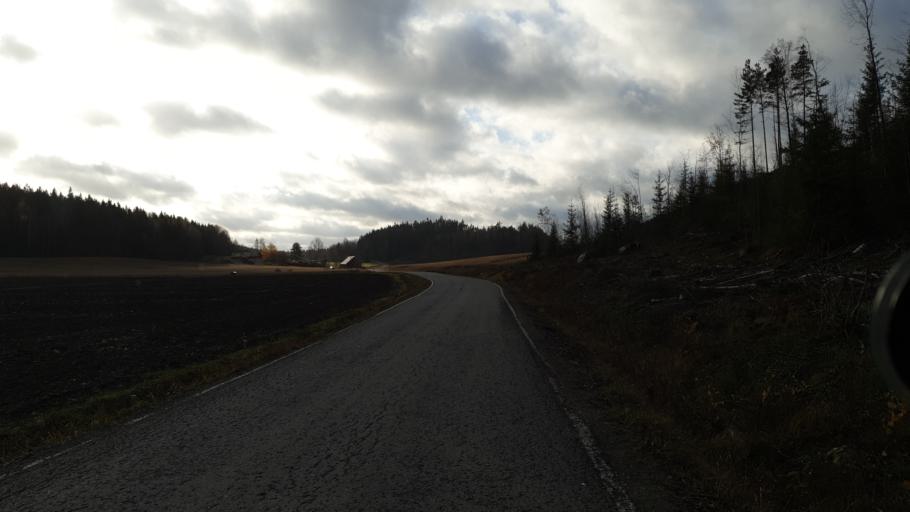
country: FI
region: Uusimaa
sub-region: Helsinki
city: Siuntio
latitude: 60.2580
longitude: 24.2990
